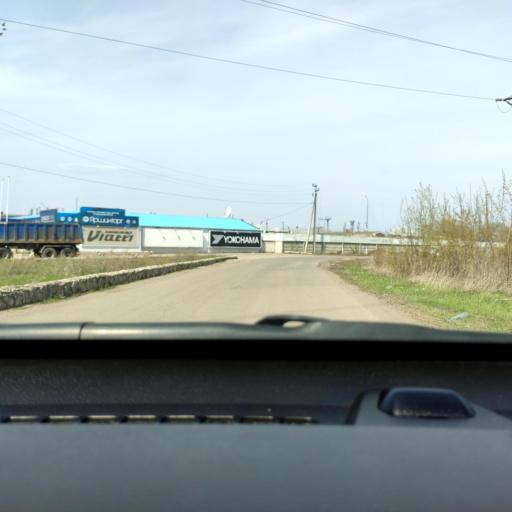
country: RU
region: Samara
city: Tol'yatti
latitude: 53.5801
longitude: 49.2930
